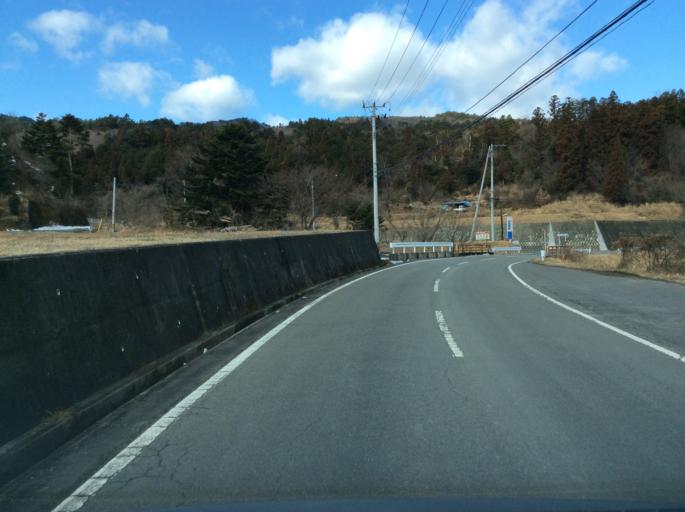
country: JP
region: Fukushima
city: Iwaki
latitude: 37.1798
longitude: 140.9484
